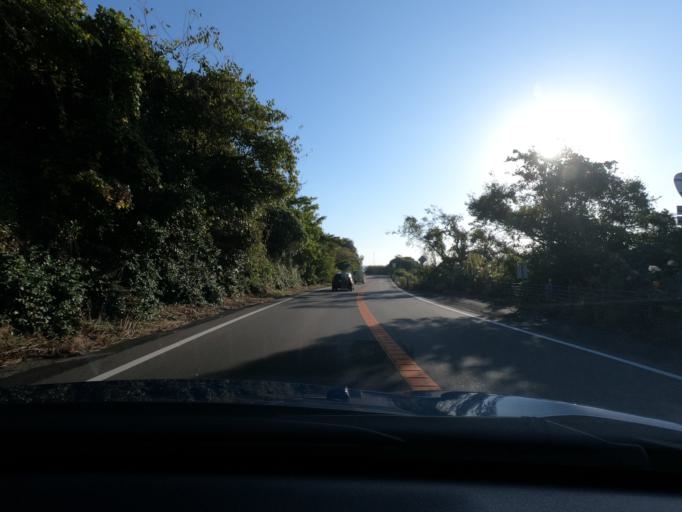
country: JP
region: Kagoshima
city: Akune
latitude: 31.9524
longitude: 130.2164
